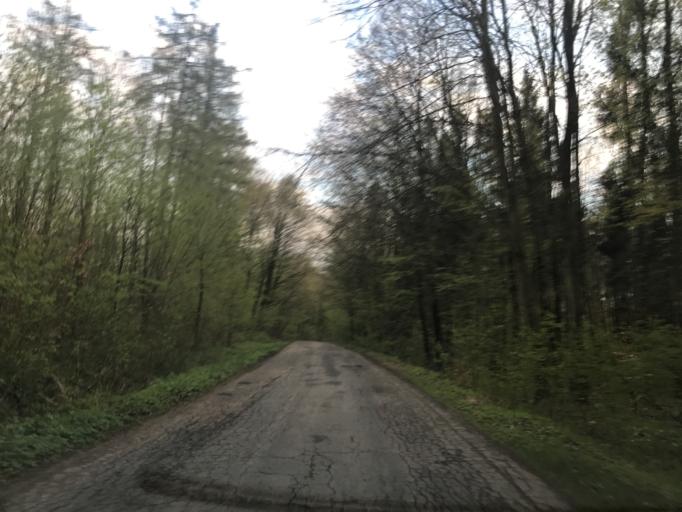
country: PL
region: Warmian-Masurian Voivodeship
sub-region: Powiat ilawski
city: Lubawa
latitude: 53.5475
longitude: 19.8976
